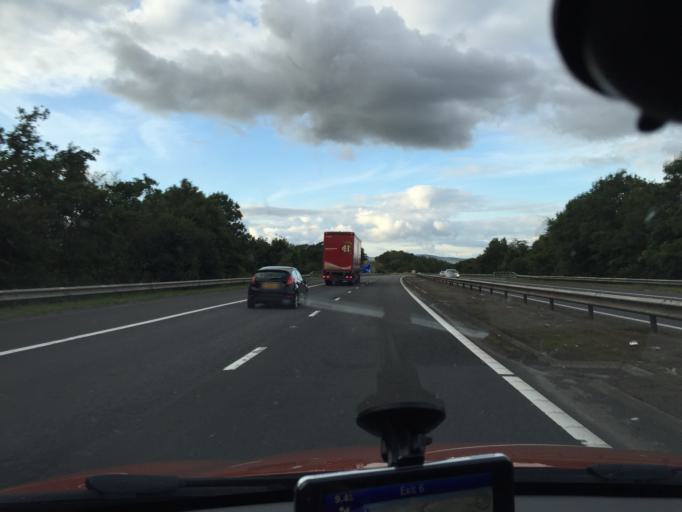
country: GB
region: Scotland
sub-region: North Lanarkshire
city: Glenboig
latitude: 55.9019
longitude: -4.0681
